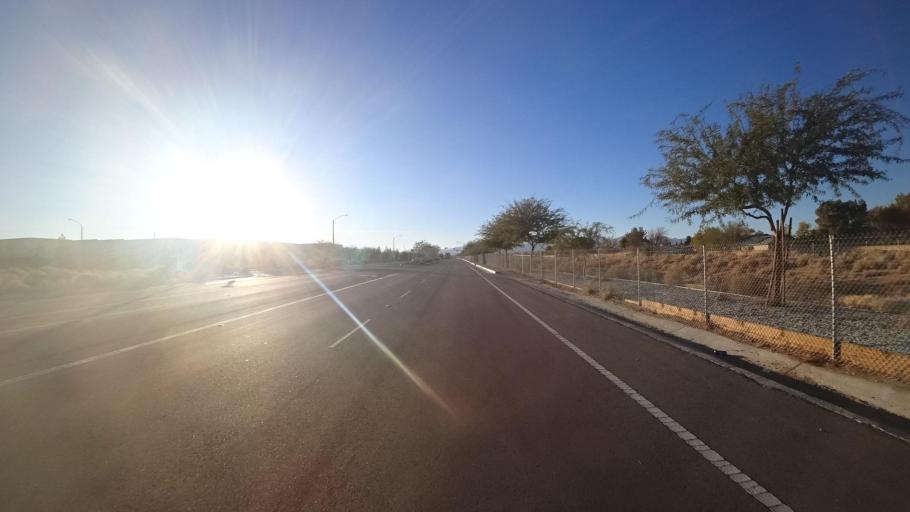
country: US
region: California
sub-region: Kern County
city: Ridgecrest
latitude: 35.6080
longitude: -117.6652
